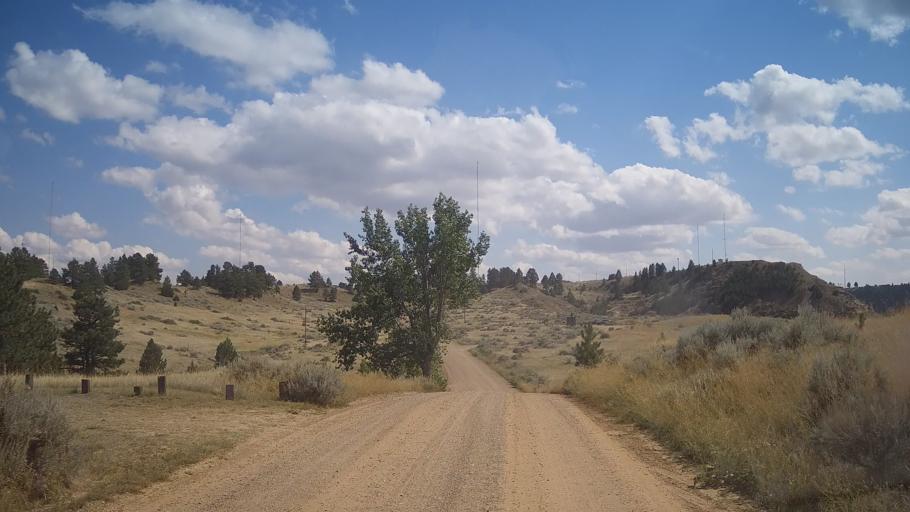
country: US
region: Montana
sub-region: Dawson County
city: Glendive
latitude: 47.0565
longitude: -104.6812
